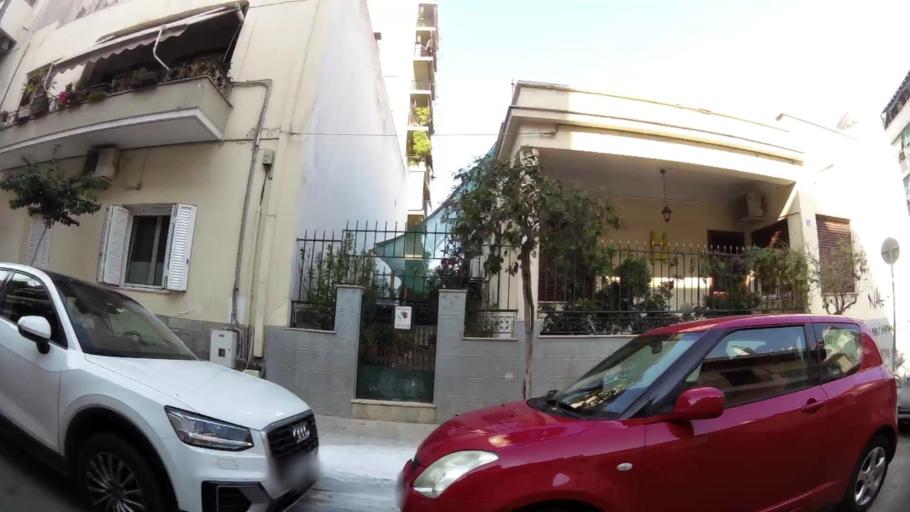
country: GR
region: Attica
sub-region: Nomarchia Athinas
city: Athens
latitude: 37.9707
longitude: 23.7061
